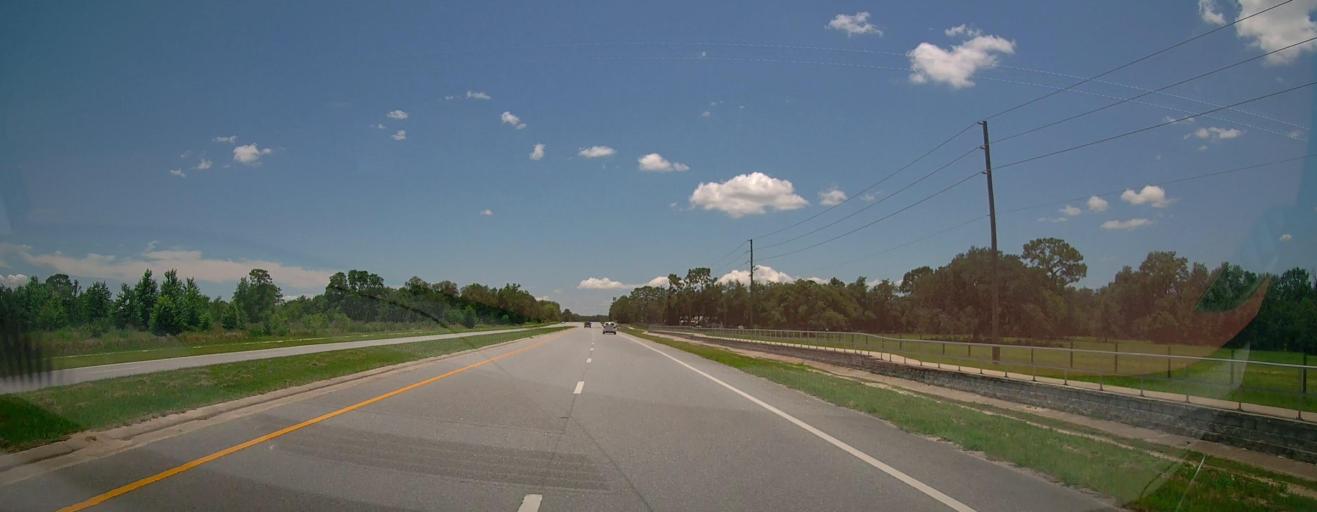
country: US
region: Florida
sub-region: Marion County
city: Belleview
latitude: 29.0498
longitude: -82.0175
